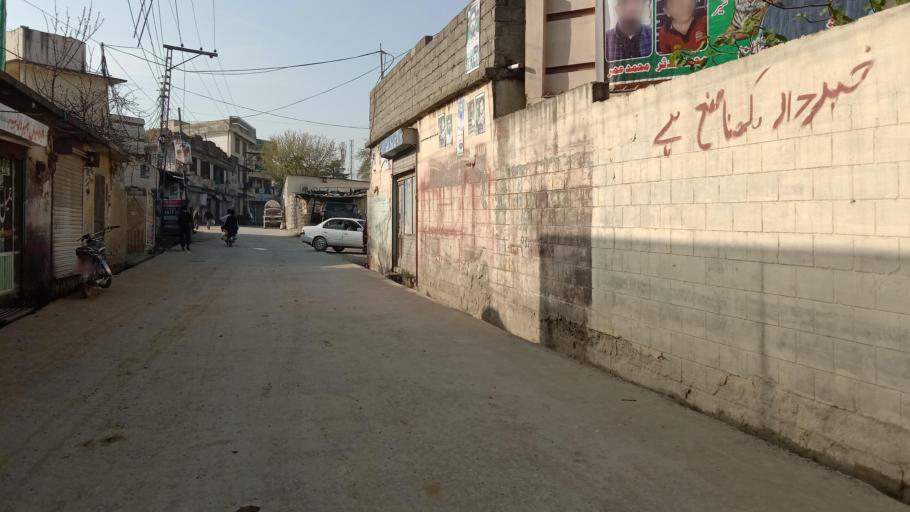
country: PK
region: Khyber Pakhtunkhwa
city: Abbottabad
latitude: 34.1980
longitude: 73.2292
